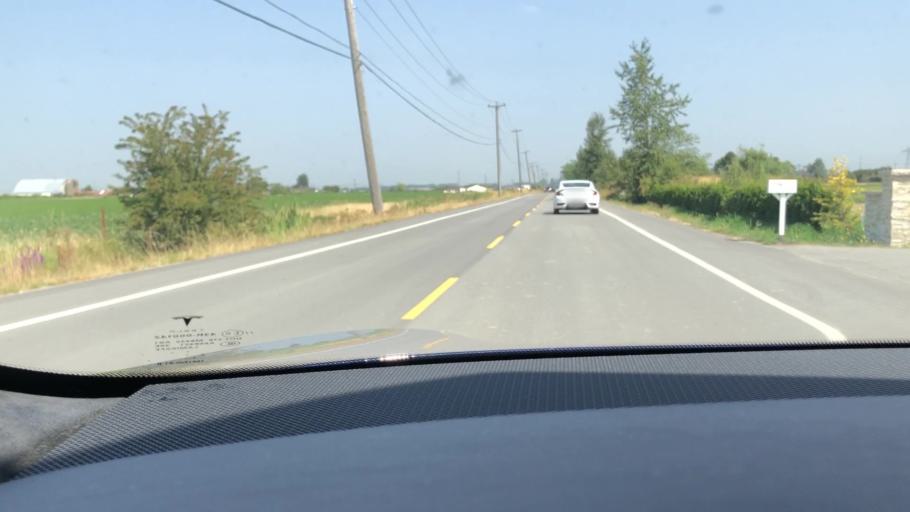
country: CA
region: British Columbia
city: Ladner
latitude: 49.0493
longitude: -123.0797
